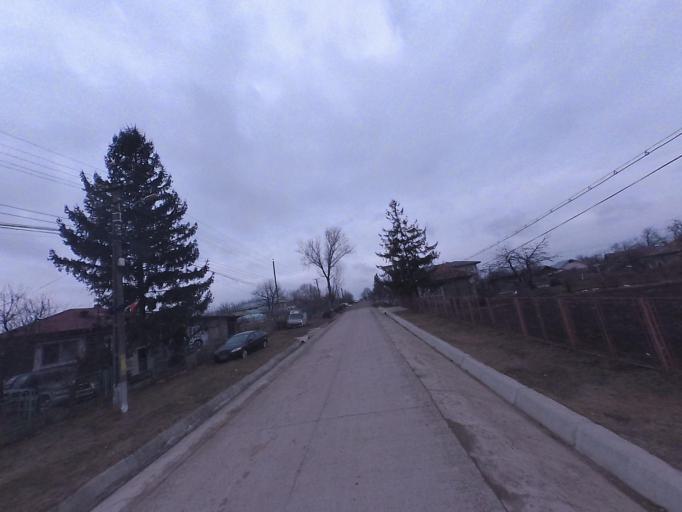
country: RO
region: Iasi
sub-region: Comuna Popricani
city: Popricani
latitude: 47.2908
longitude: 27.5061
